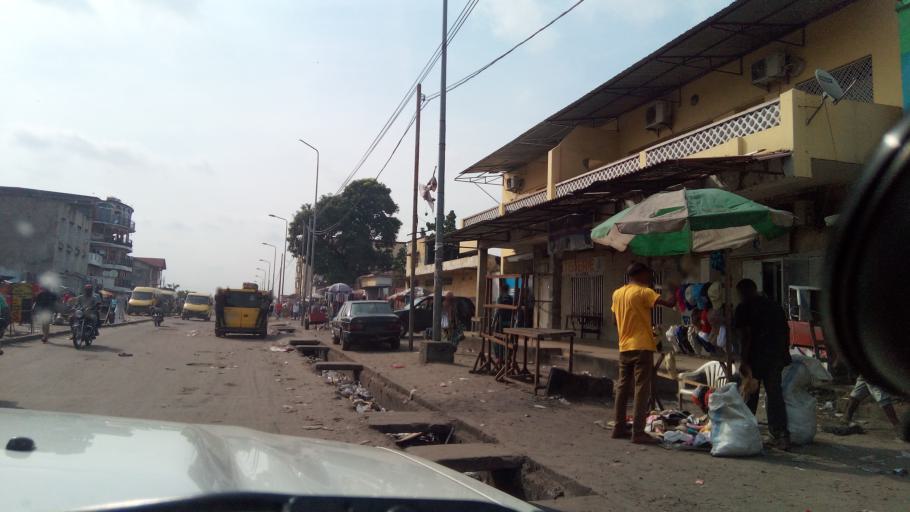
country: CD
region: Kinshasa
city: Kinshasa
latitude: -4.3470
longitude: 15.3124
